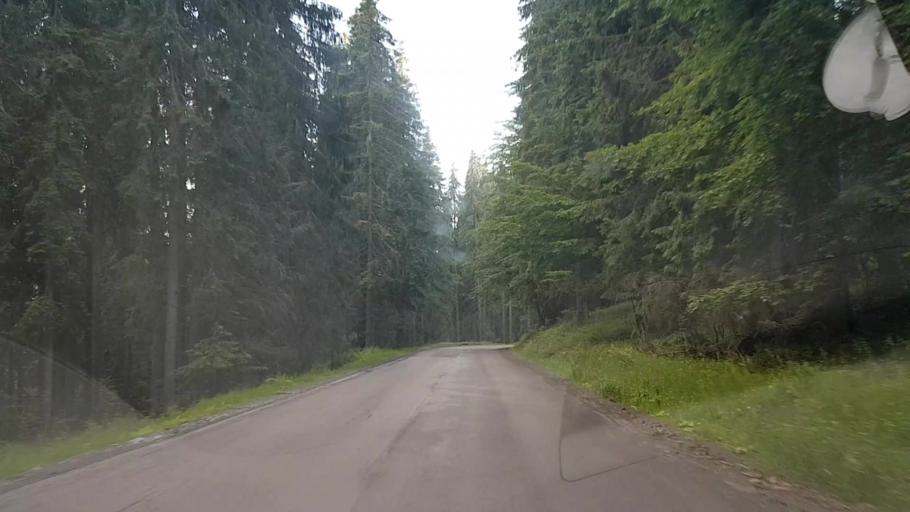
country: RO
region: Harghita
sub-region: Comuna Varsag
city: Varsag
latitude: 46.6510
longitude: 25.2900
